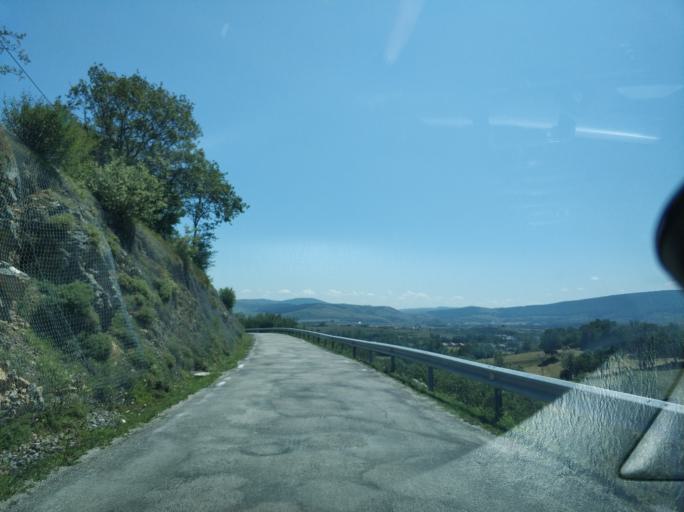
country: ES
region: Cantabria
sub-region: Provincia de Cantabria
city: Reinosa
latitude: 43.0252
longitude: -4.1690
